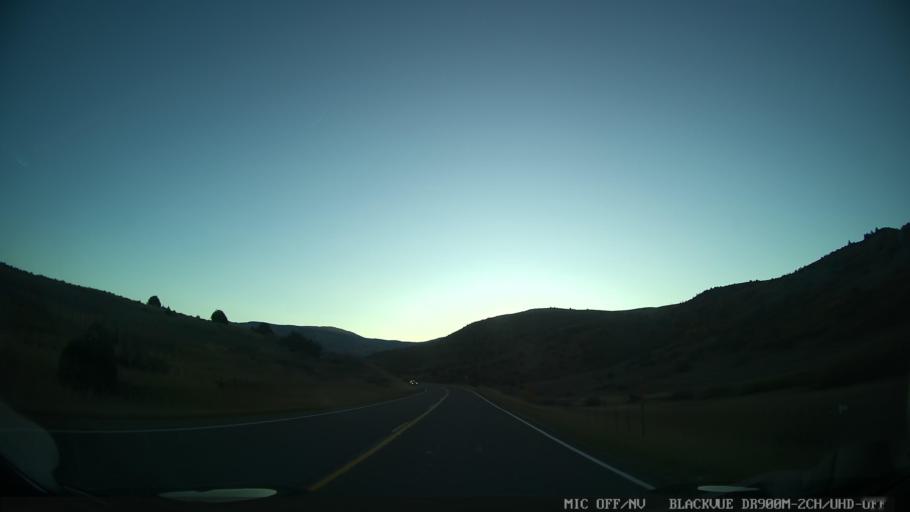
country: US
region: Colorado
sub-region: Eagle County
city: Edwards
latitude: 39.8175
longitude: -106.6554
